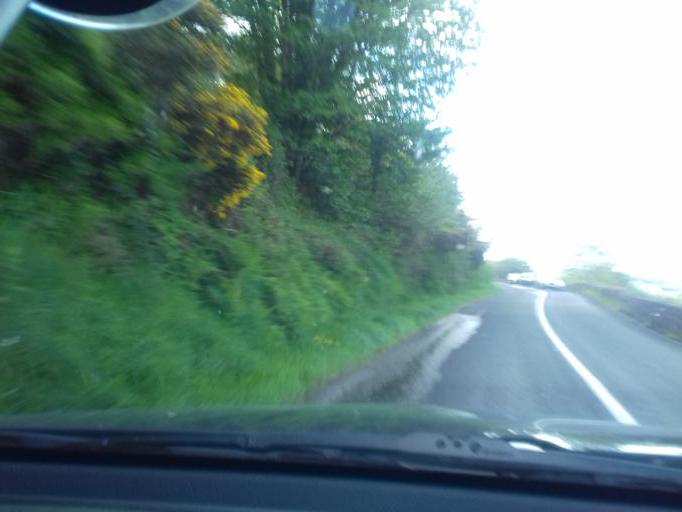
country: IE
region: Munster
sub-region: Waterford
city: Dunmore East
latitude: 52.2423
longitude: -6.9820
